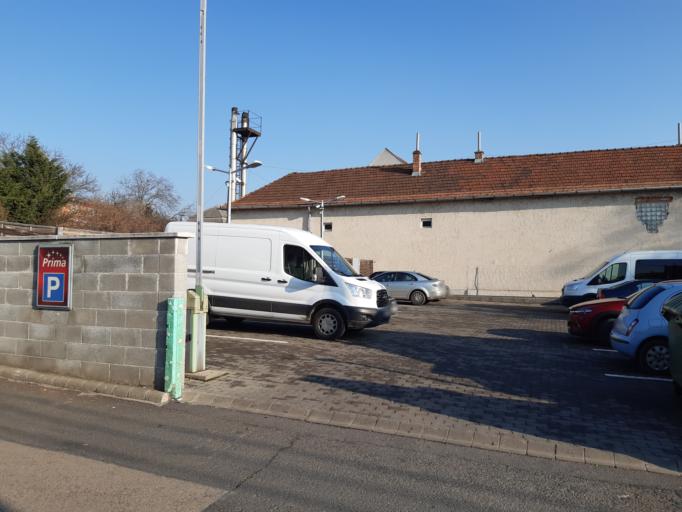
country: HU
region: Pest
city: Budaors
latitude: 47.4614
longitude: 18.9578
